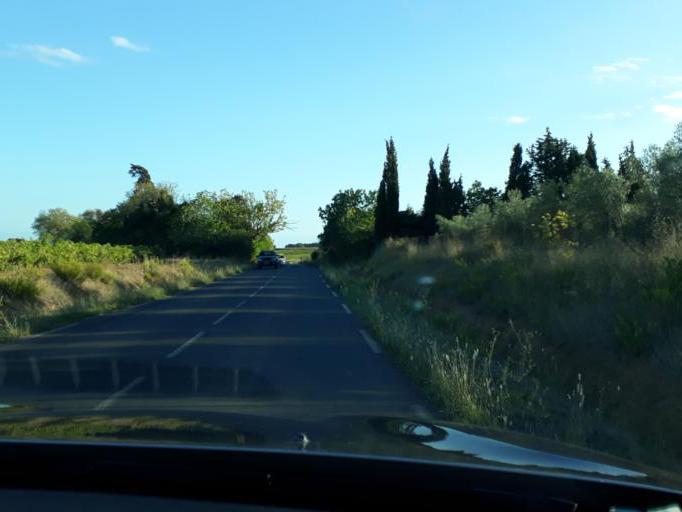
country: FR
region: Languedoc-Roussillon
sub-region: Departement de l'Herault
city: Pomerols
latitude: 43.3831
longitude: 3.4984
